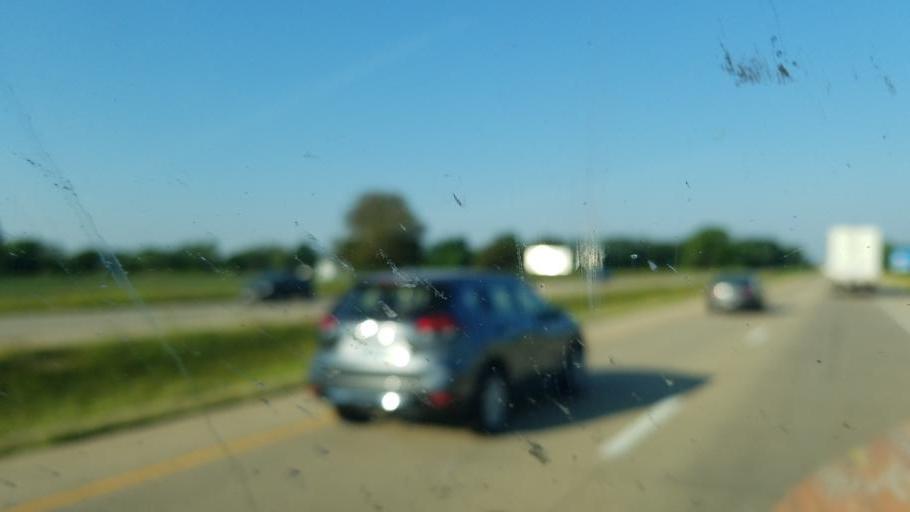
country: US
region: Illinois
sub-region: Grundy County
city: Morris
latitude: 41.4048
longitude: -88.3939
